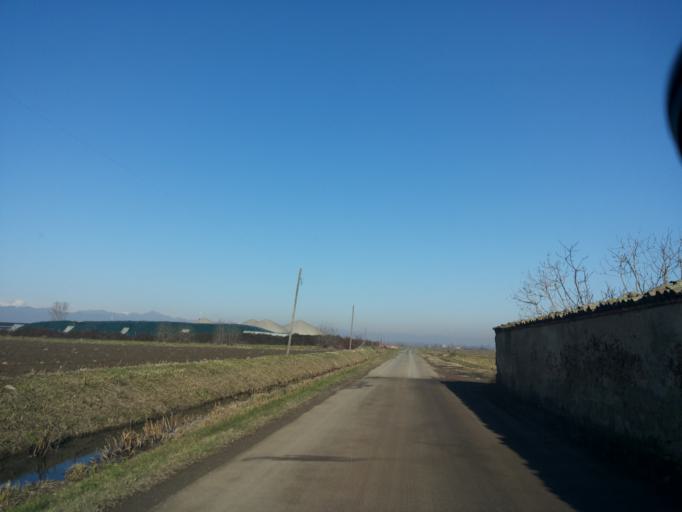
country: IT
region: Piedmont
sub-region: Provincia di Vercelli
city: San Germano Vercellese
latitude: 45.3716
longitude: 8.2414
